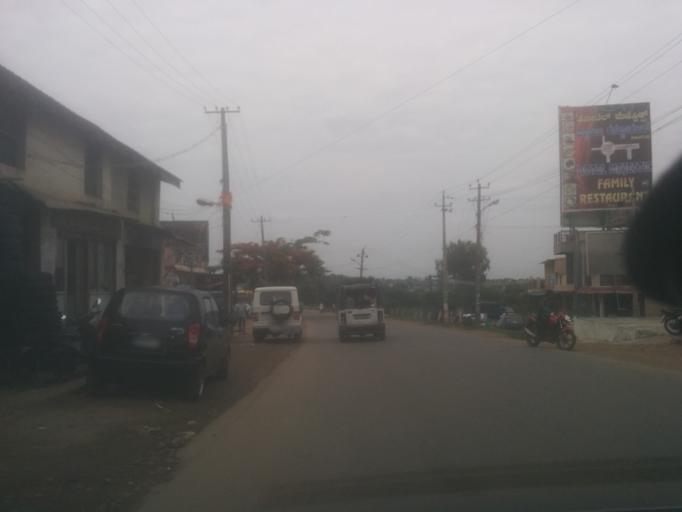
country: IN
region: Karnataka
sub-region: Hassan
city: Belur
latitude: 13.1670
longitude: 75.8698
